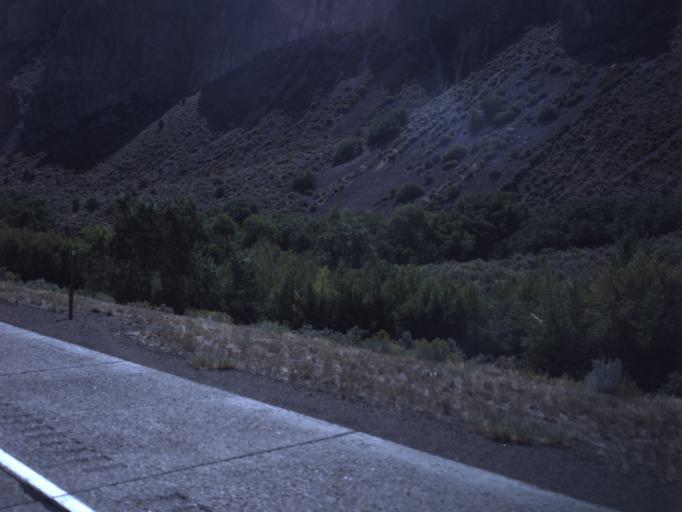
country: US
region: Utah
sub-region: Sevier County
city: Monroe
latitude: 38.5792
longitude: -112.2992
